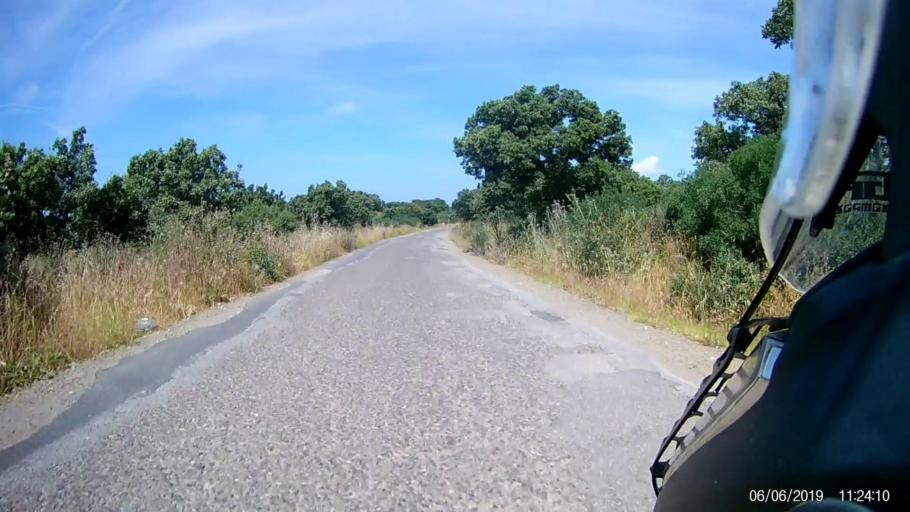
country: TR
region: Canakkale
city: Gulpinar
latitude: 39.6216
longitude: 26.1741
